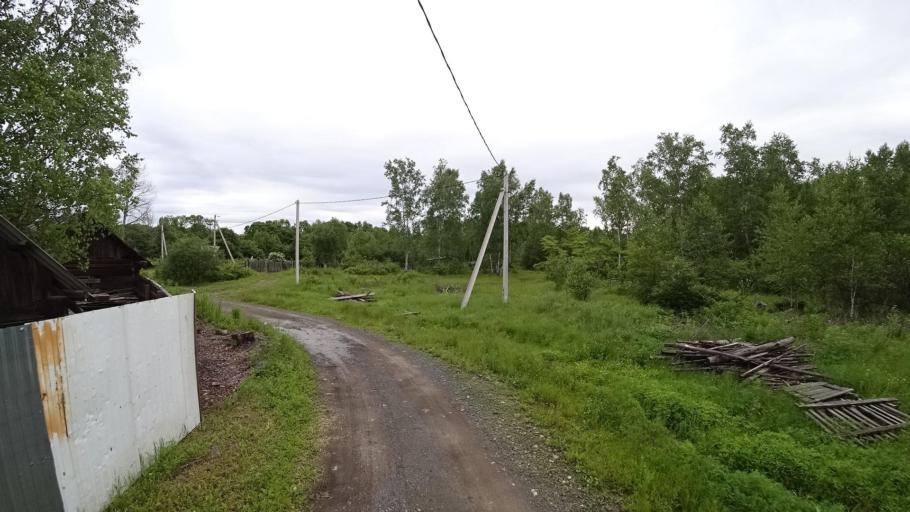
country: RU
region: Khabarovsk Krai
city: Amursk
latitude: 49.9041
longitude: 136.1357
